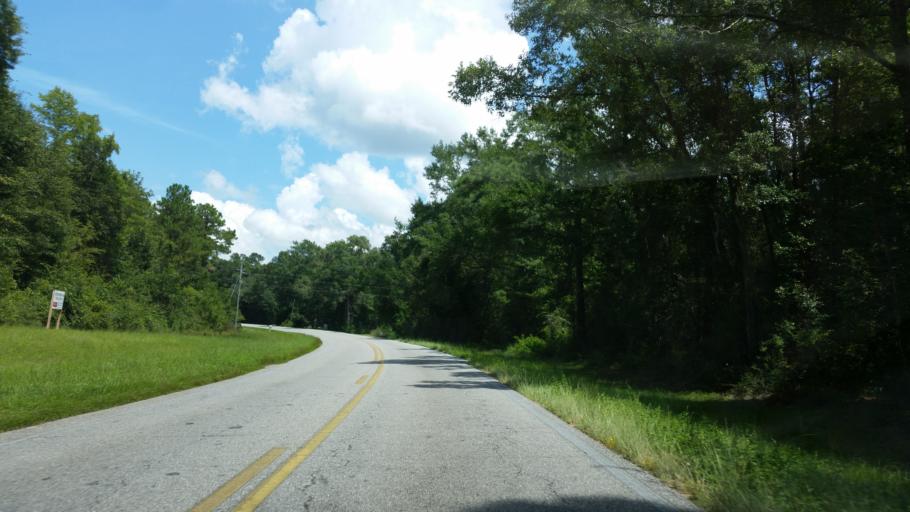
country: US
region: Florida
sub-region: Santa Rosa County
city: Milton
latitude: 30.6430
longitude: -87.0181
